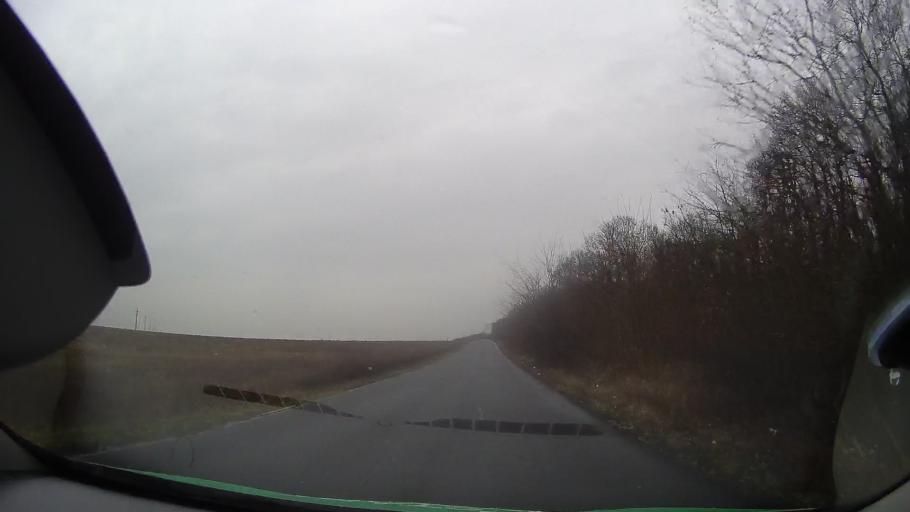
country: RO
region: Bihor
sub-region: Comuna Tinca
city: Gurbediu
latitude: 46.7762
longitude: 21.8800
